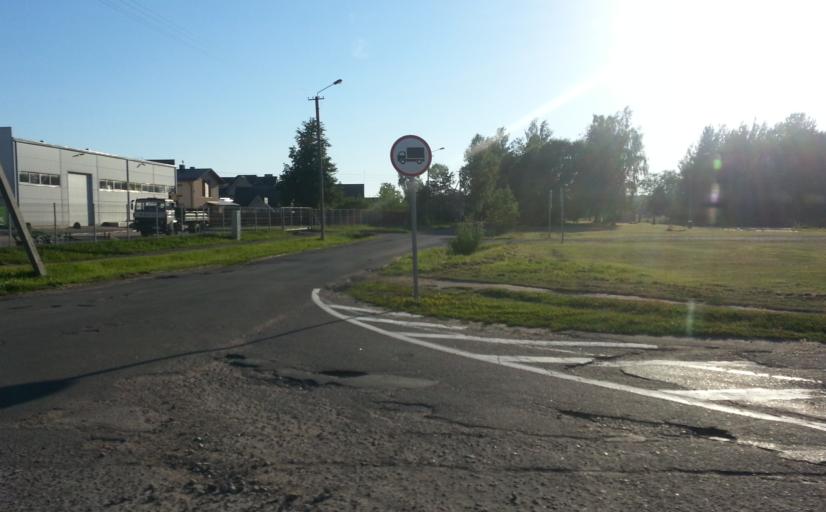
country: LT
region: Panevezys
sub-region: Panevezys City
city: Panevezys
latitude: 55.7573
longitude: 24.3685
